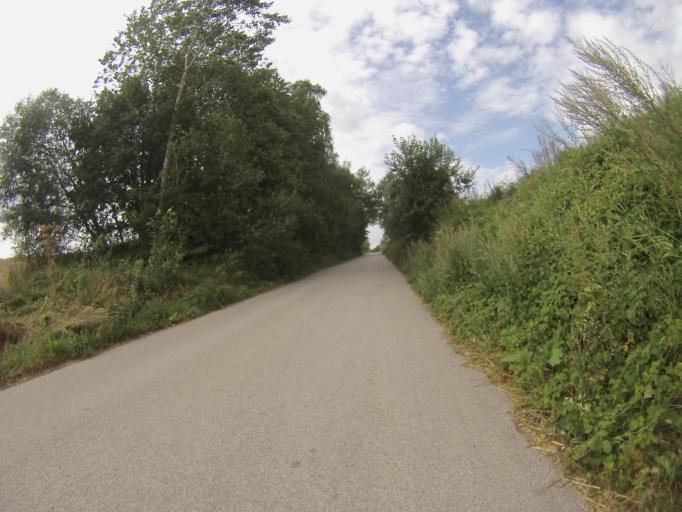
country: PL
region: Swietokrzyskie
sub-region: Powiat kielecki
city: Lagow
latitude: 50.7402
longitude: 21.1270
